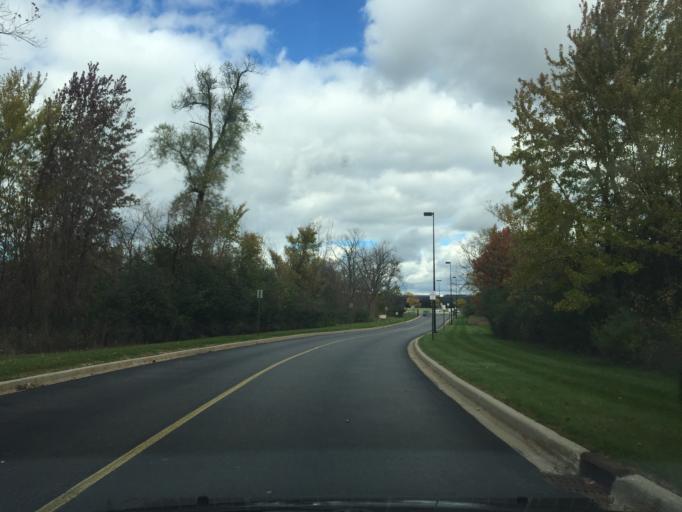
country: US
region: Michigan
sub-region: Oakland County
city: Auburn Hills
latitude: 42.6473
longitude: -83.2347
